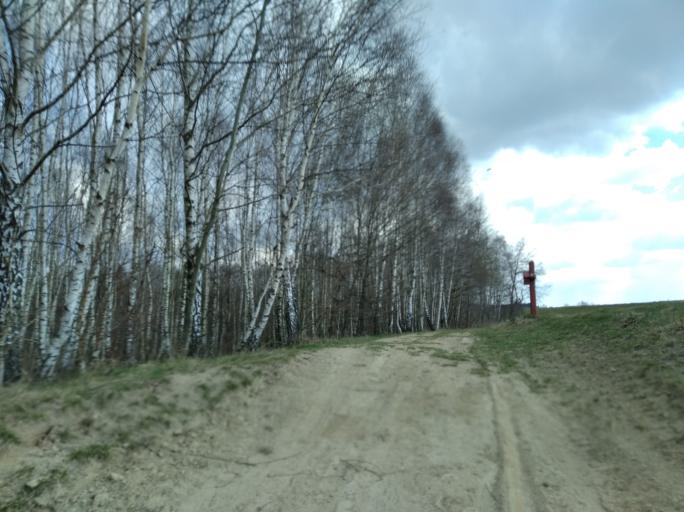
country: PL
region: Subcarpathian Voivodeship
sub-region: Powiat strzyzowski
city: Strzyzow
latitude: 49.9110
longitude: 21.7523
